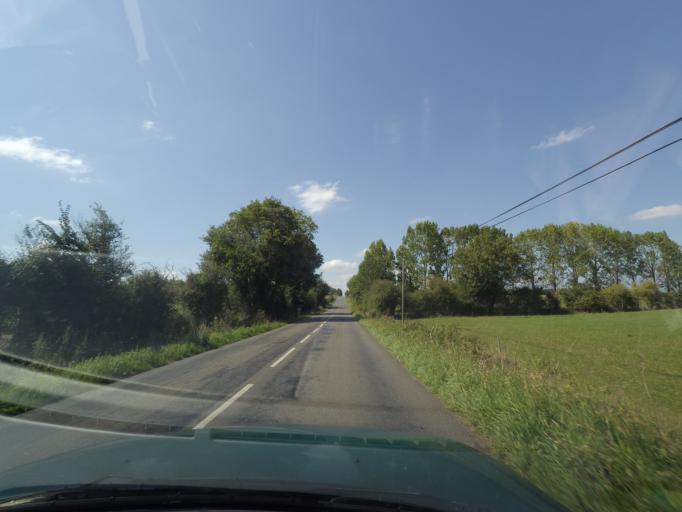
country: FR
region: Pays de la Loire
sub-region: Departement de la Loire-Atlantique
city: Saint-Lumine-de-Coutais
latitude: 47.0405
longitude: -1.7099
